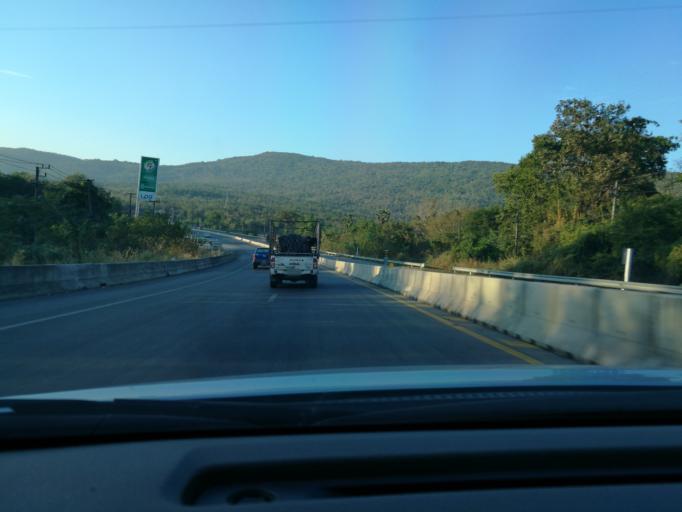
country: TH
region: Phitsanulok
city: Wang Thong
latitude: 16.8606
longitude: 100.5036
